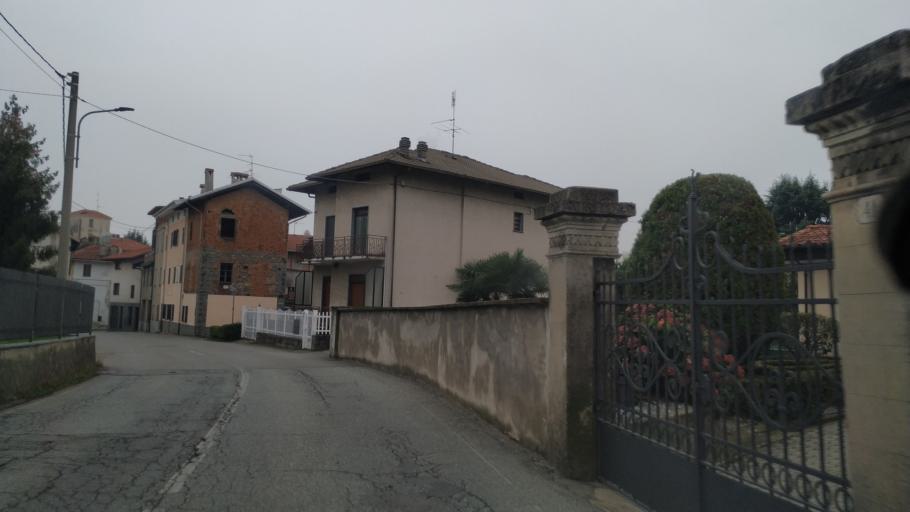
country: IT
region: Piedmont
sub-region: Provincia di Biella
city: Lessona
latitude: 45.5820
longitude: 8.1908
